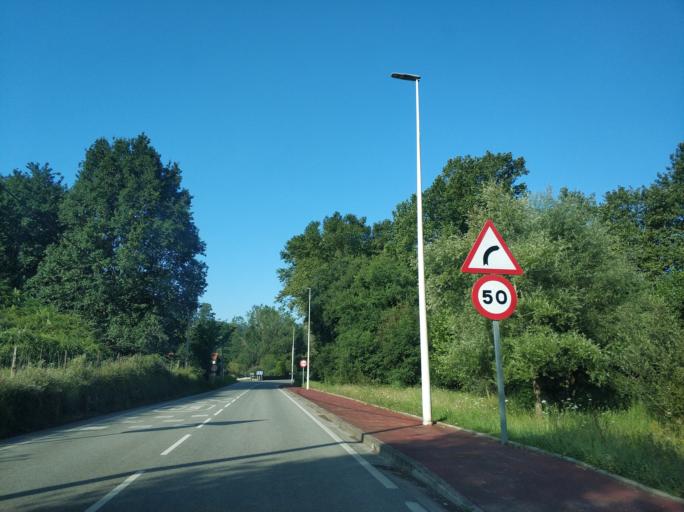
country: ES
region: Cantabria
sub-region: Provincia de Cantabria
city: Miengo
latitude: 43.3915
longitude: -3.9487
